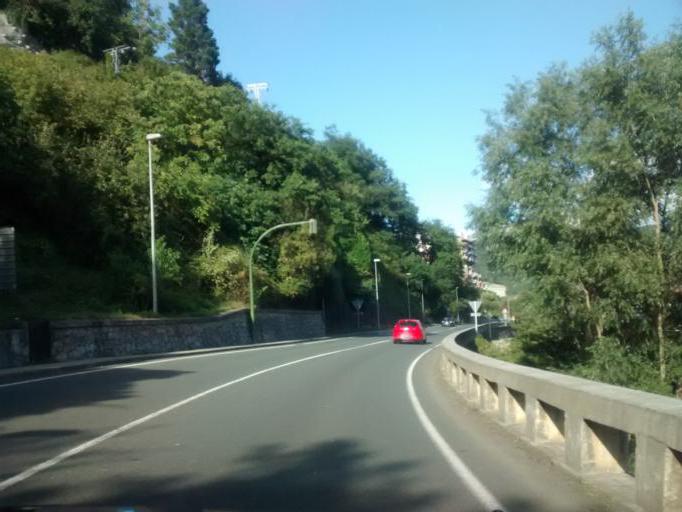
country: ES
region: Basque Country
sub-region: Provincia de Guipuzcoa
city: Elgoibar
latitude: 43.2157
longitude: -2.4168
